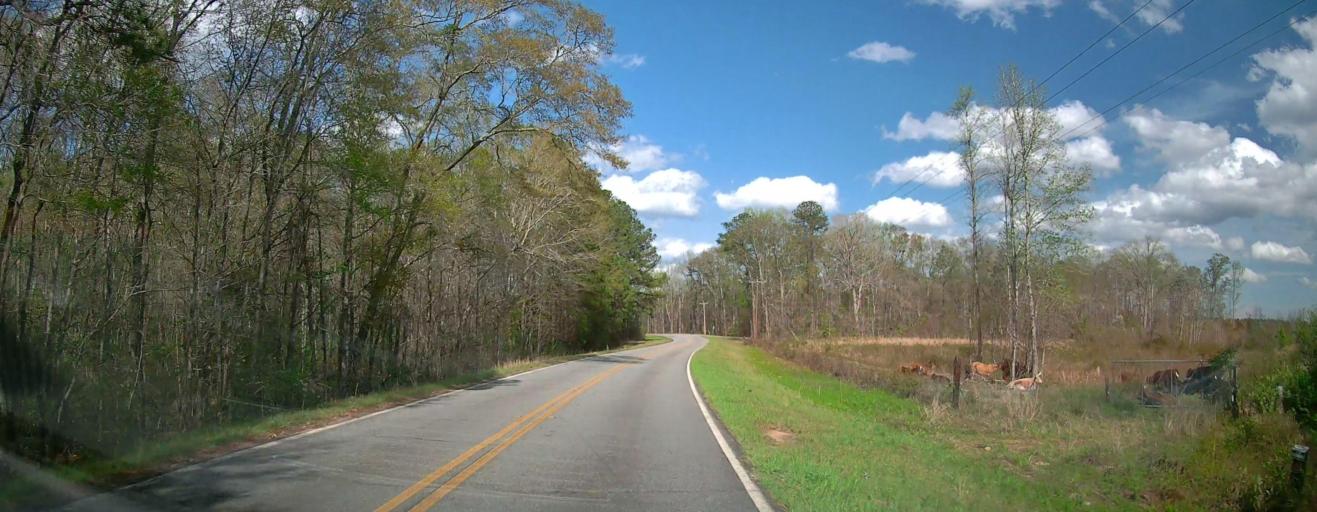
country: US
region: Georgia
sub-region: Wilkinson County
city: Gordon
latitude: 32.8048
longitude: -83.4152
